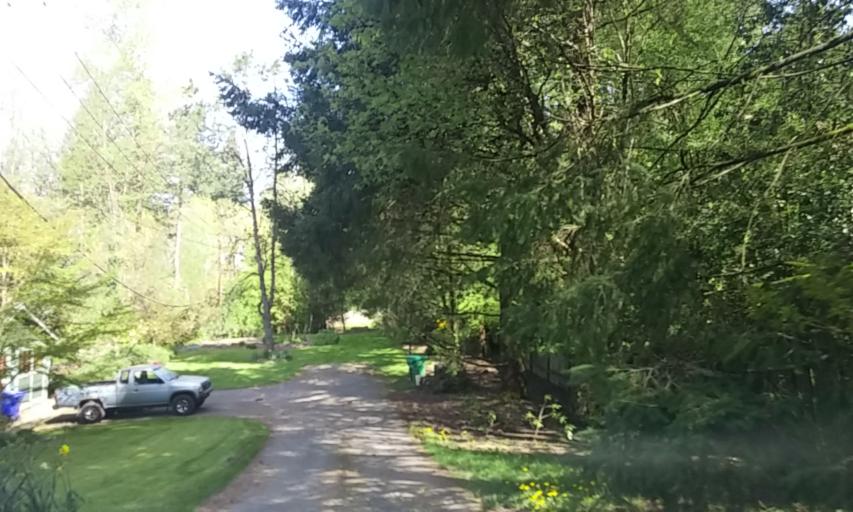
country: US
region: Oregon
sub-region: Washington County
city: West Haven-Sylvan
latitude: 45.5167
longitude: -122.7369
